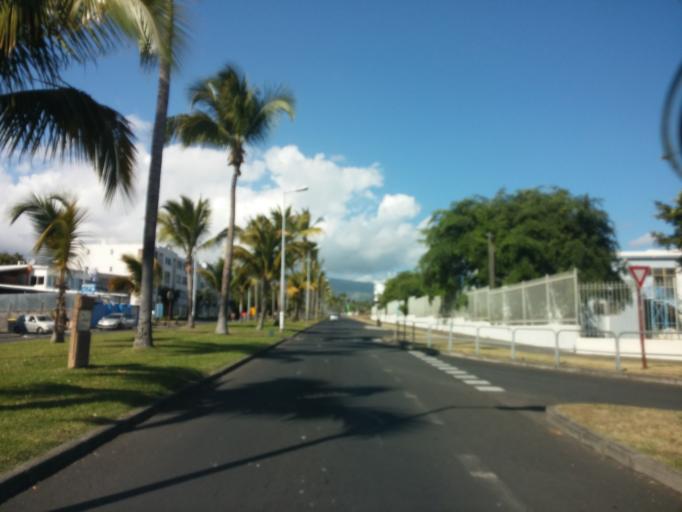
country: RE
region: Reunion
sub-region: Reunion
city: Le Port
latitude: -20.9429
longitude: 55.2921
